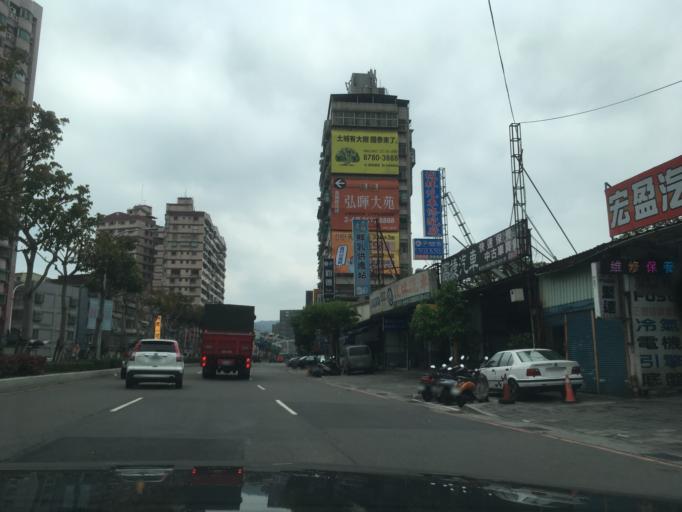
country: TW
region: Taipei
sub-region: Taipei
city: Banqiao
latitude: 24.9785
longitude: 121.4393
